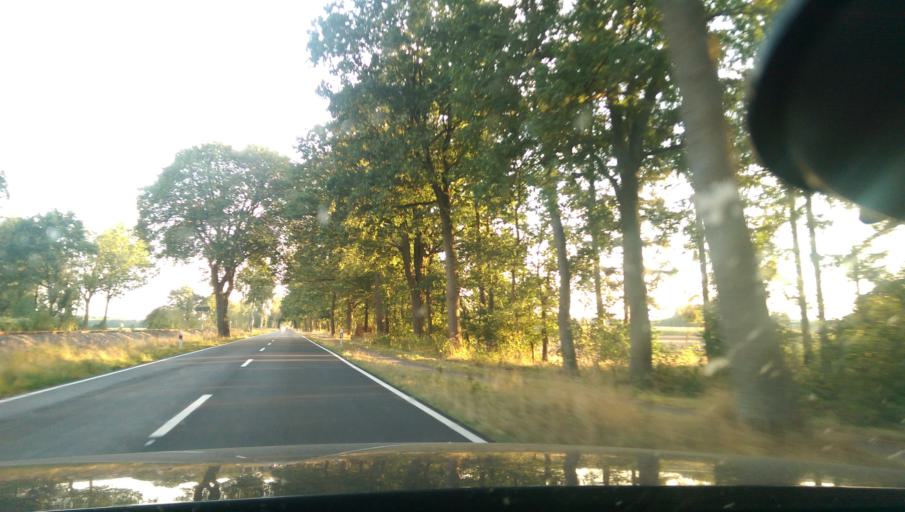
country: DE
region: Lower Saxony
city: Walsrode
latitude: 52.8080
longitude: 9.5934
